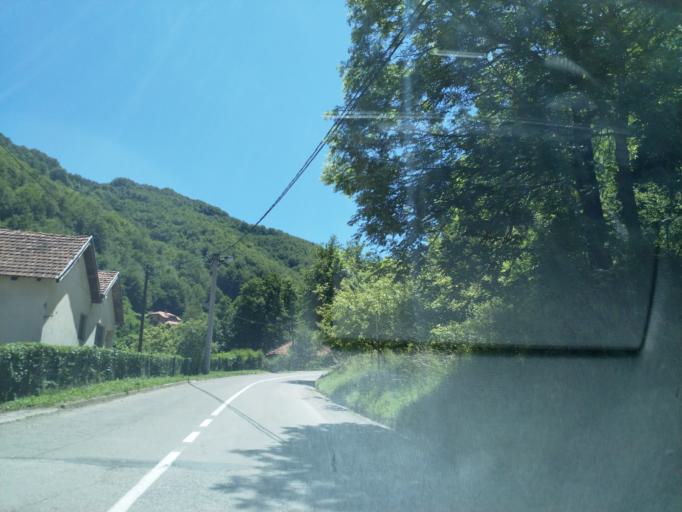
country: XK
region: Mitrovica
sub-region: Komuna e Leposaviqit
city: Leposaviq
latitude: 43.3006
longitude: 20.8852
